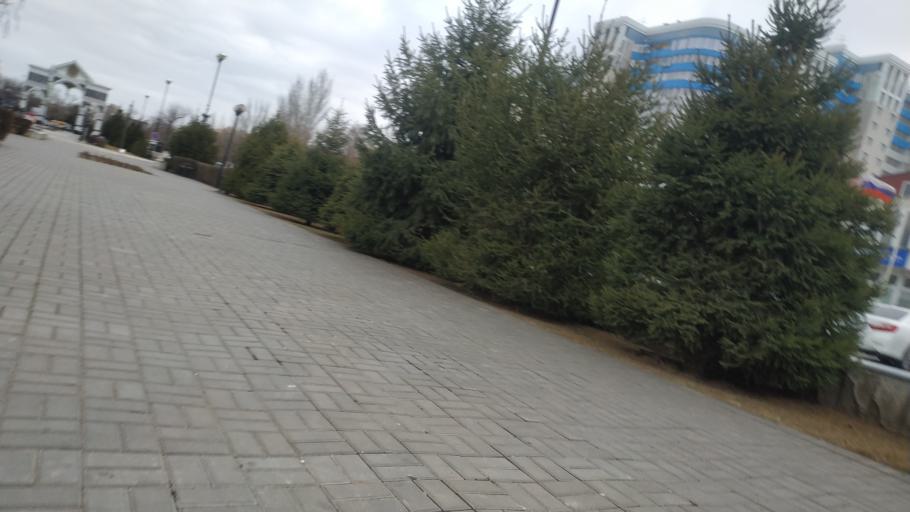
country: RU
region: Astrakhan
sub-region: Gorod Astrakhan'
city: Astrakhan'
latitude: 46.3459
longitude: 48.0186
